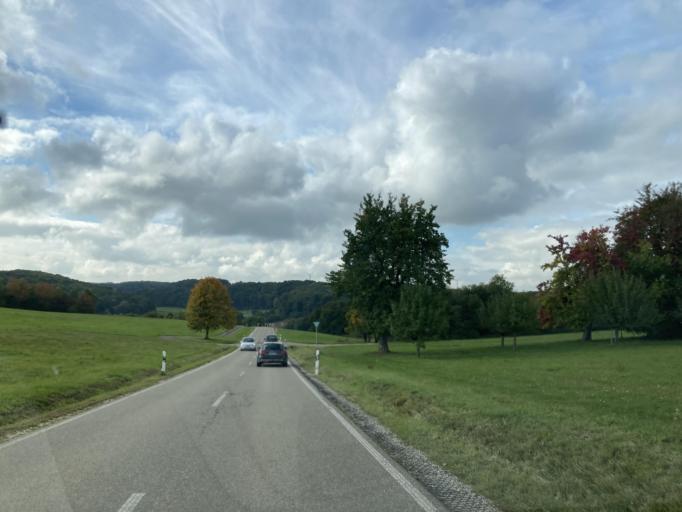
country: DE
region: Baden-Wuerttemberg
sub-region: Regierungsbezirk Stuttgart
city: Hohenstadt
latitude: 48.5461
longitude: 9.6566
